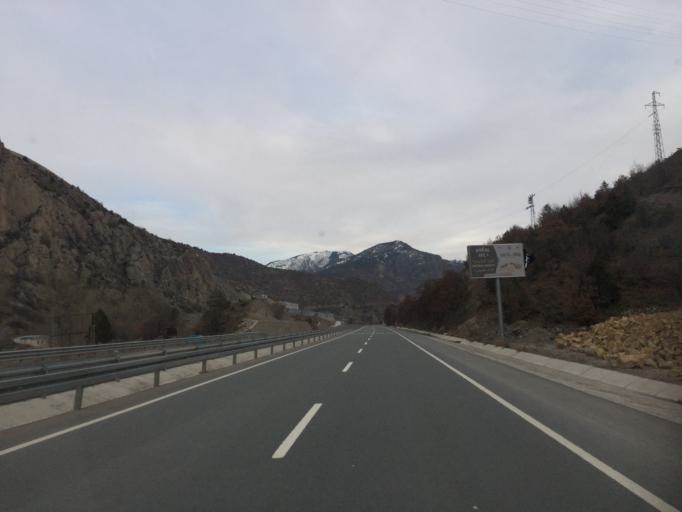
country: TR
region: Gumushane
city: Torul
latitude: 40.5326
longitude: 39.3358
